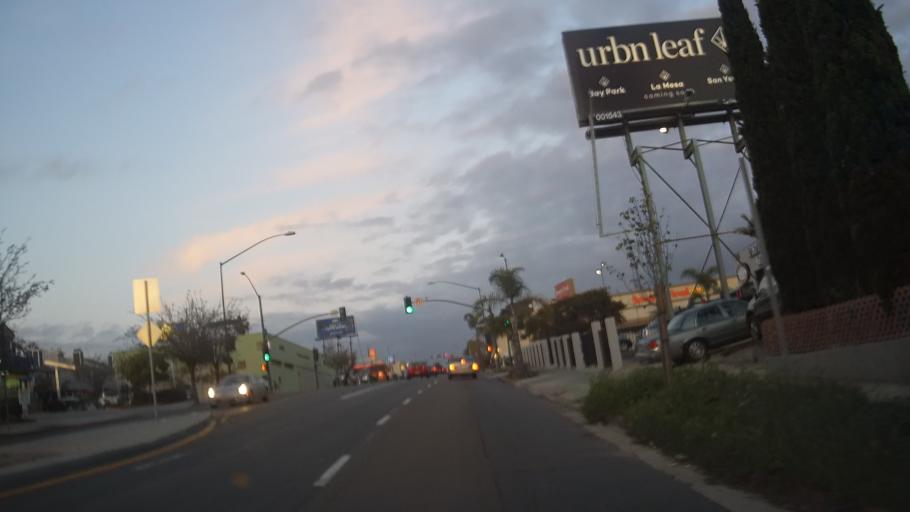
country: US
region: California
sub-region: San Diego County
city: San Diego
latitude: 32.7484
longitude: -117.1422
